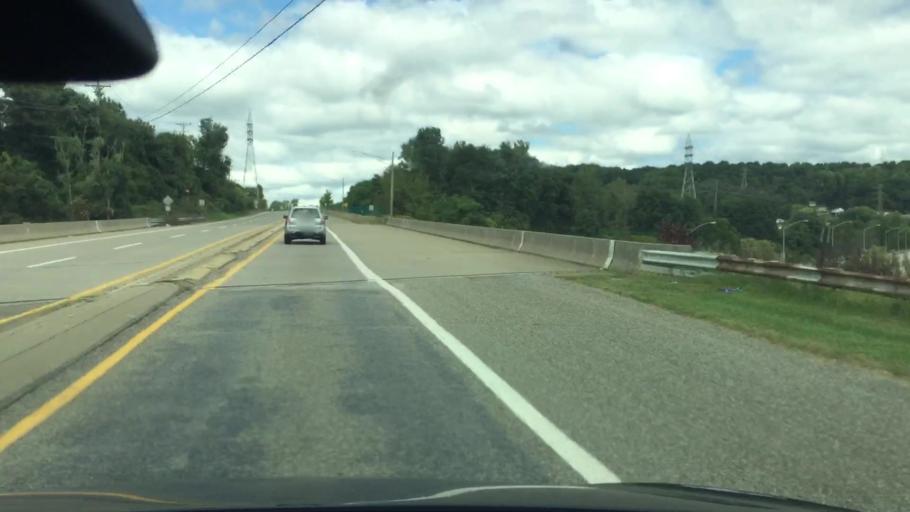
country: US
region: Pennsylvania
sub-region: Allegheny County
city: Cheswick
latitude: 40.5492
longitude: -79.8193
